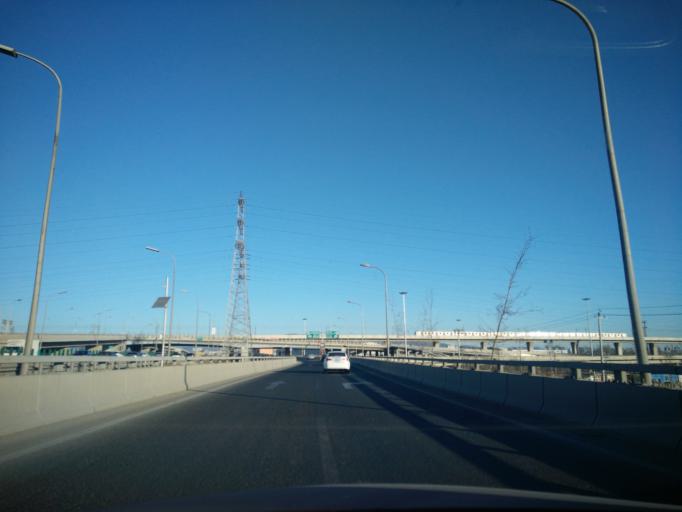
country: CN
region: Beijing
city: Lugu
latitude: 39.8616
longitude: 116.2104
